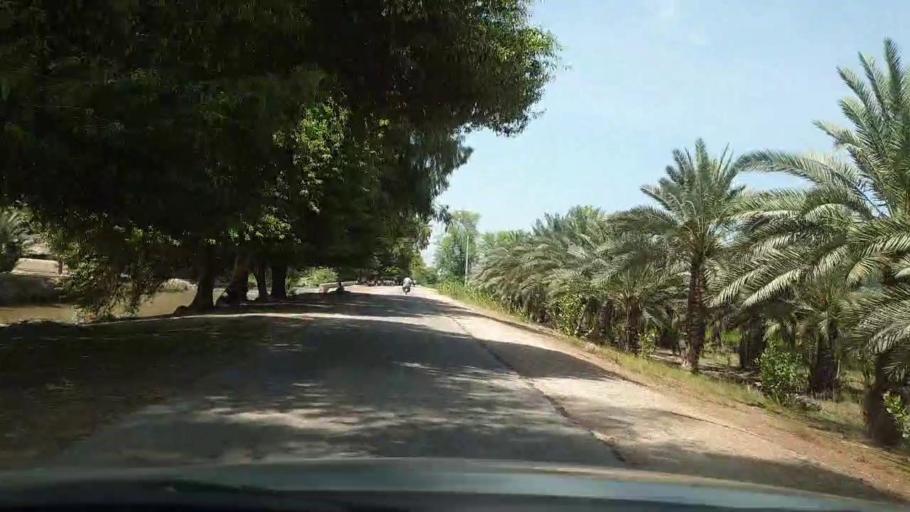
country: PK
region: Sindh
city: Pano Aqil
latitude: 27.6995
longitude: 69.1119
